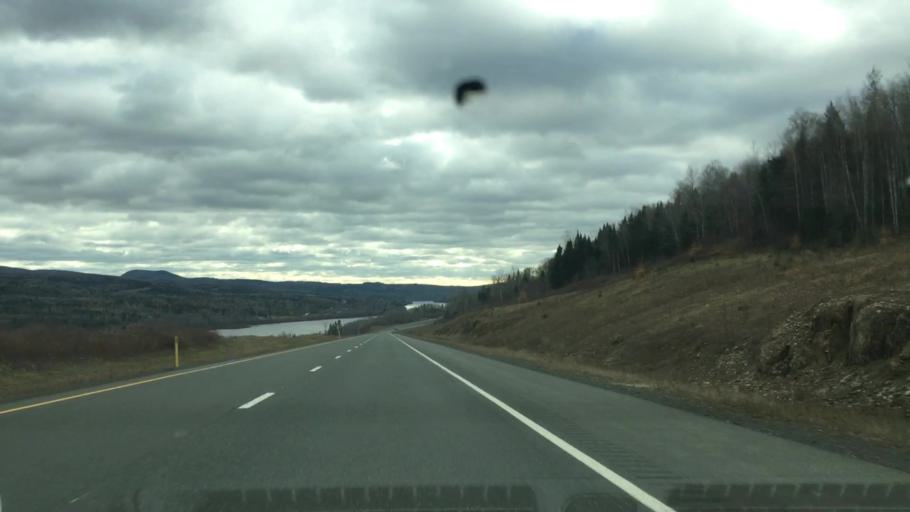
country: US
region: Maine
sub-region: Aroostook County
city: Fort Fairfield
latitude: 46.6879
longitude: -67.7362
